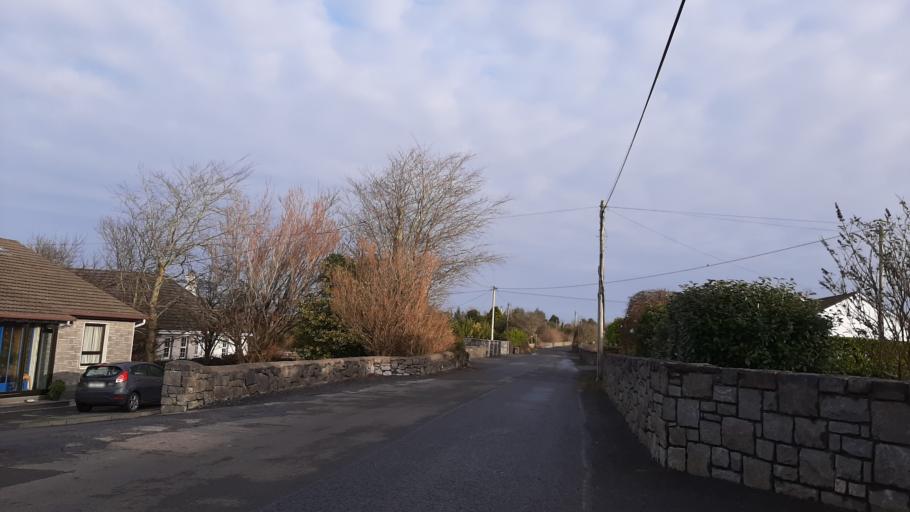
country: IE
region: Connaught
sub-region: County Galway
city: Gaillimh
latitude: 53.3052
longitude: -9.0626
